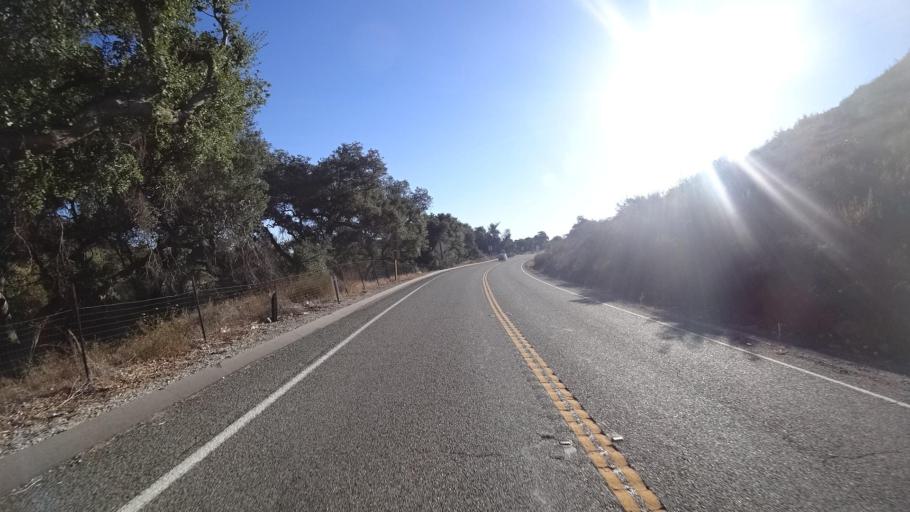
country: MX
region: Baja California
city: Tecate
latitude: 32.6088
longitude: -116.6290
